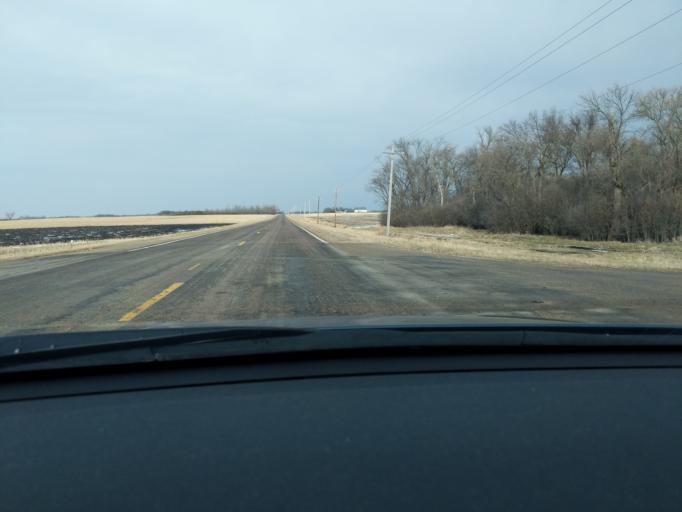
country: US
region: Minnesota
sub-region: Renville County
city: Renville
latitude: 44.7452
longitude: -95.3407
